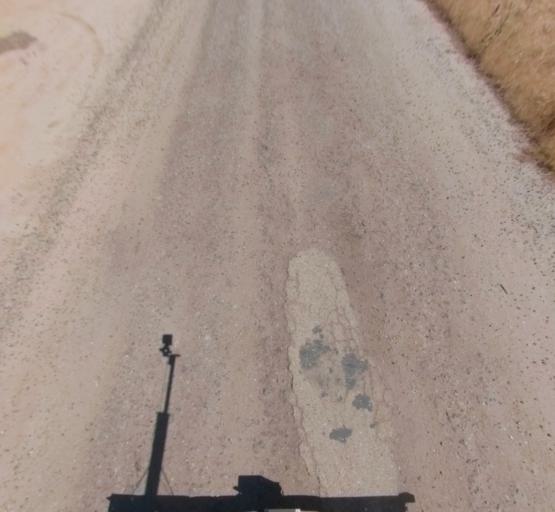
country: US
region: California
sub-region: Madera County
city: Bonadelle Ranchos-Madera Ranchos
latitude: 36.8784
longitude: -119.8526
